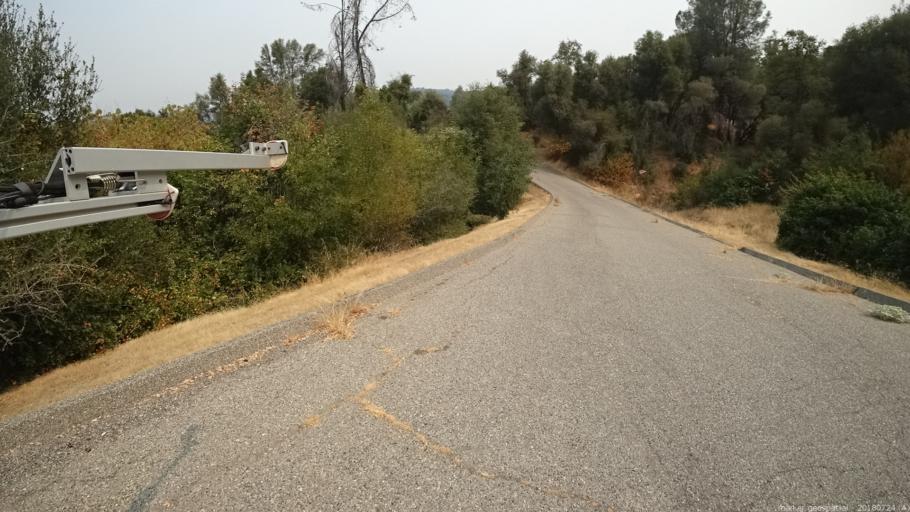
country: US
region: California
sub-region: Madera County
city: Oakhurst
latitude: 37.3263
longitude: -119.6200
